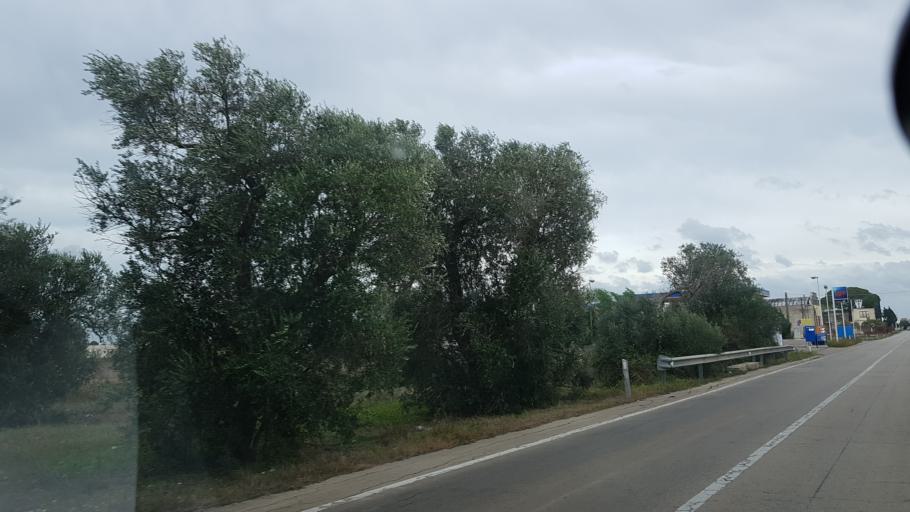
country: IT
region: Apulia
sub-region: Provincia di Lecce
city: Guagnano
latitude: 40.3997
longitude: 17.9368
